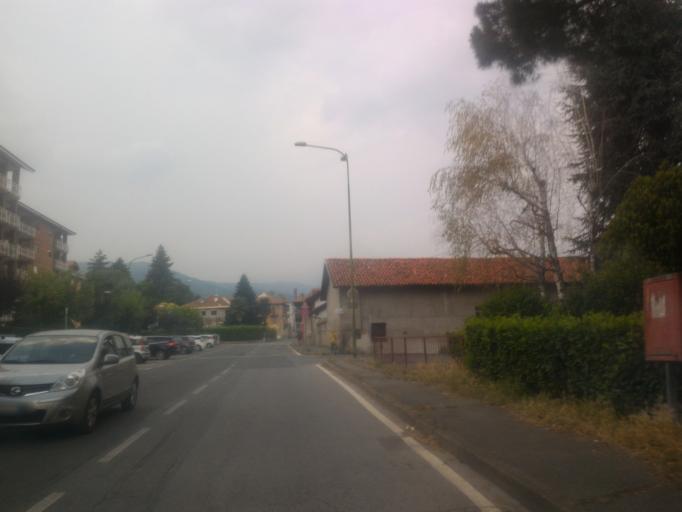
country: IT
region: Piedmont
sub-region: Provincia di Torino
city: Pinerolo
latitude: 44.8783
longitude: 7.3238
